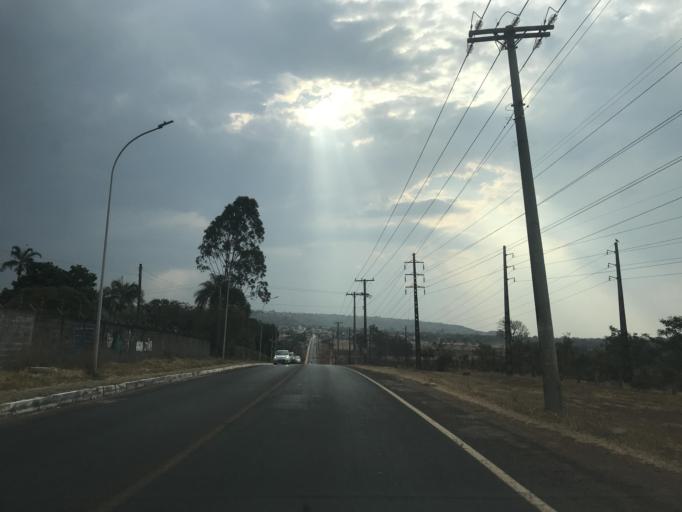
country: BR
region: Federal District
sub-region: Brasilia
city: Brasilia
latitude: -15.6644
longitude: -47.8223
